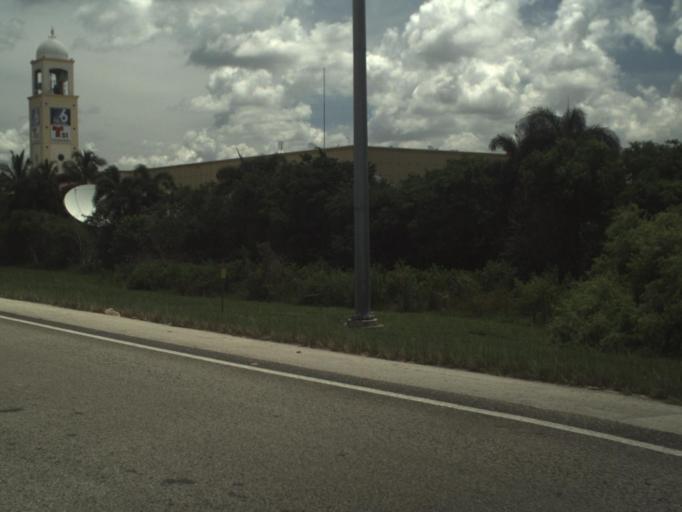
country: US
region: Florida
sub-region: Miami-Dade County
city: Country Club
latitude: 25.9840
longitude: -80.3473
